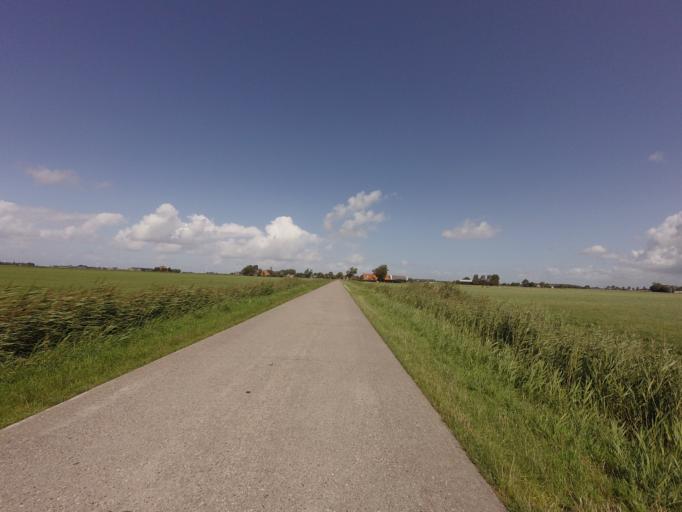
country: NL
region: Friesland
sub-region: Sudwest Fryslan
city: Makkum
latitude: 53.0738
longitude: 5.4534
